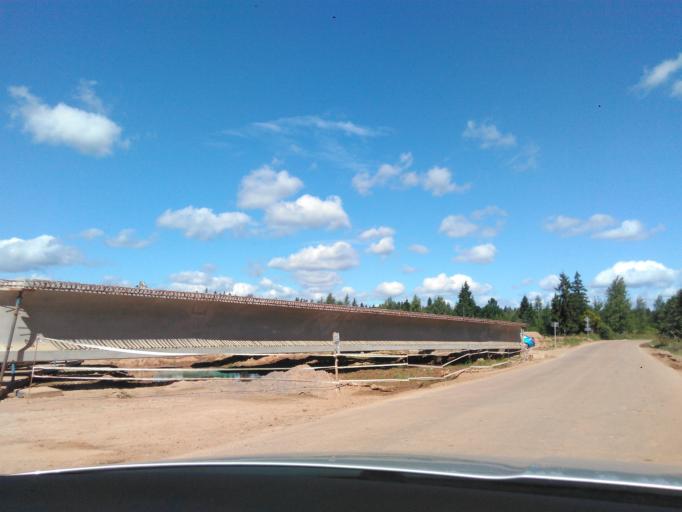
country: RU
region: Moskovskaya
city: Klin
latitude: 56.2085
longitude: 36.8106
